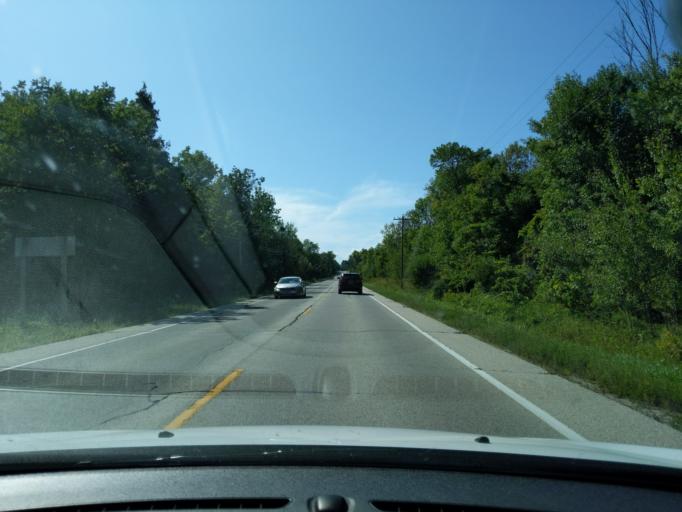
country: US
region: Michigan
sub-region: Delta County
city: Escanaba
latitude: 45.2594
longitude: -87.0522
